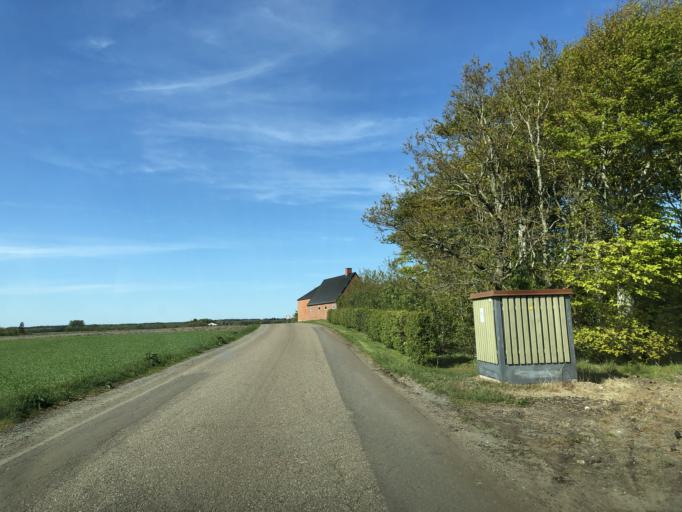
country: DK
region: Central Jutland
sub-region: Ringkobing-Skjern Kommune
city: Videbaek
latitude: 56.1767
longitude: 8.5231
